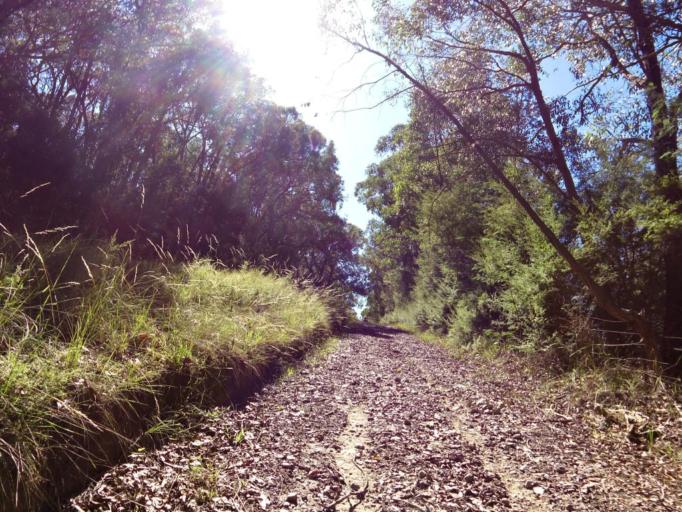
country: AU
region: Victoria
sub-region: Yarra Ranges
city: Woori Yallock
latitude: -37.7458
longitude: 145.5515
